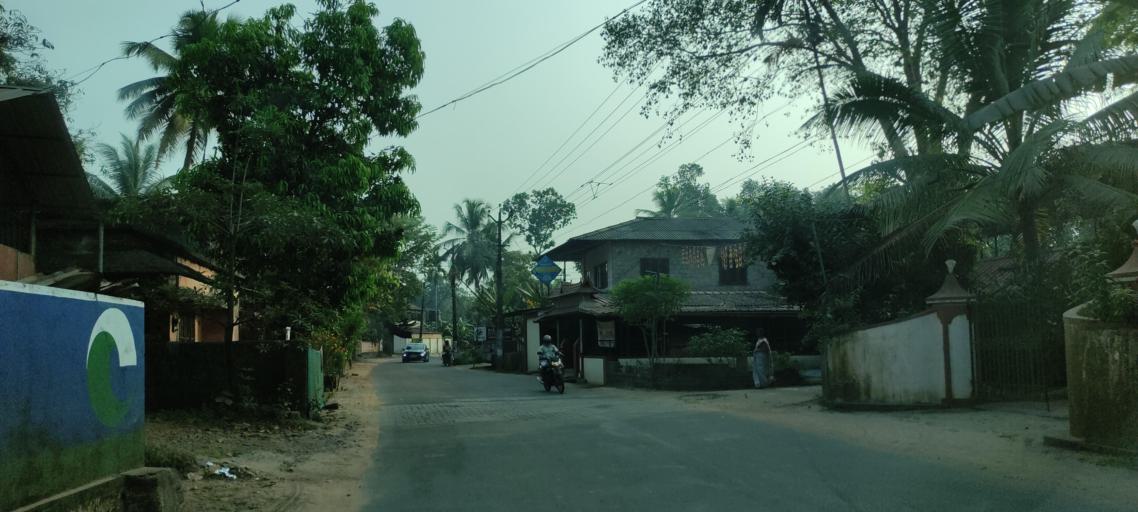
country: IN
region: Kerala
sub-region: Kottayam
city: Vaikam
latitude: 9.7042
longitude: 76.4779
